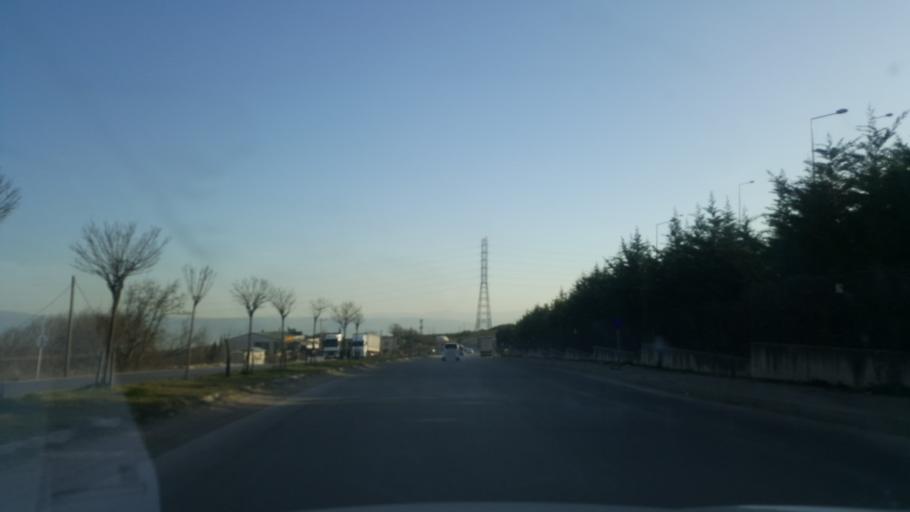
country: TR
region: Kocaeli
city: Tavsancil
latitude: 40.8118
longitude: 29.5670
